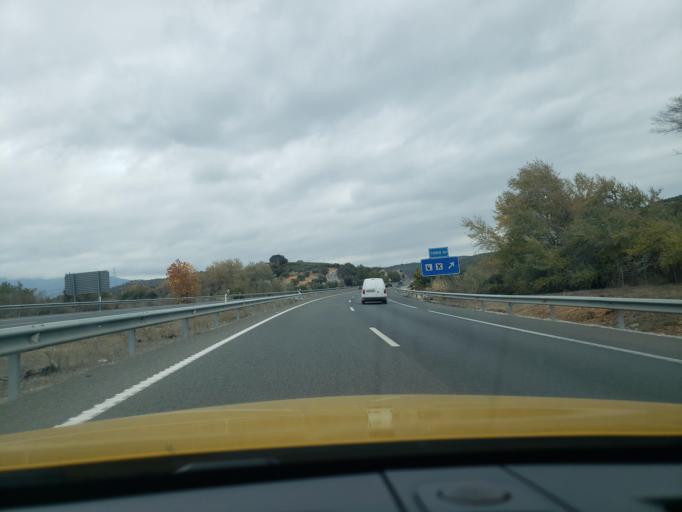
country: ES
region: Andalusia
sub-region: Provincia de Granada
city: Deifontes
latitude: 37.3328
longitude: -3.6316
